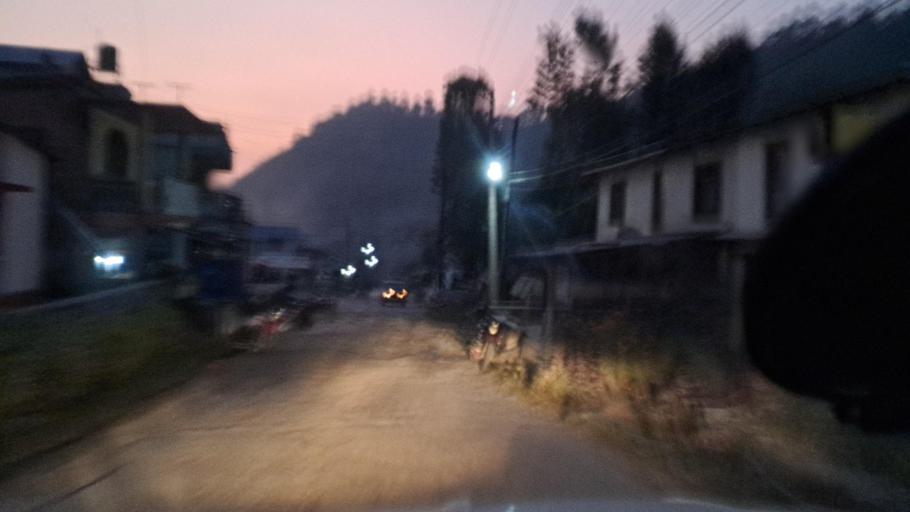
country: NP
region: Central Region
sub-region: Narayani Zone
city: Hitura
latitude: 27.5460
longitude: 85.1264
